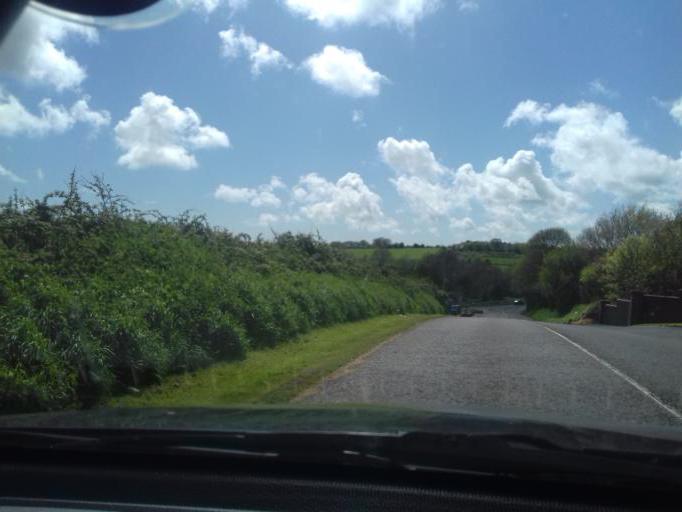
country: IE
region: Munster
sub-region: Waterford
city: Waterford
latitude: 52.2337
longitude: -7.0453
